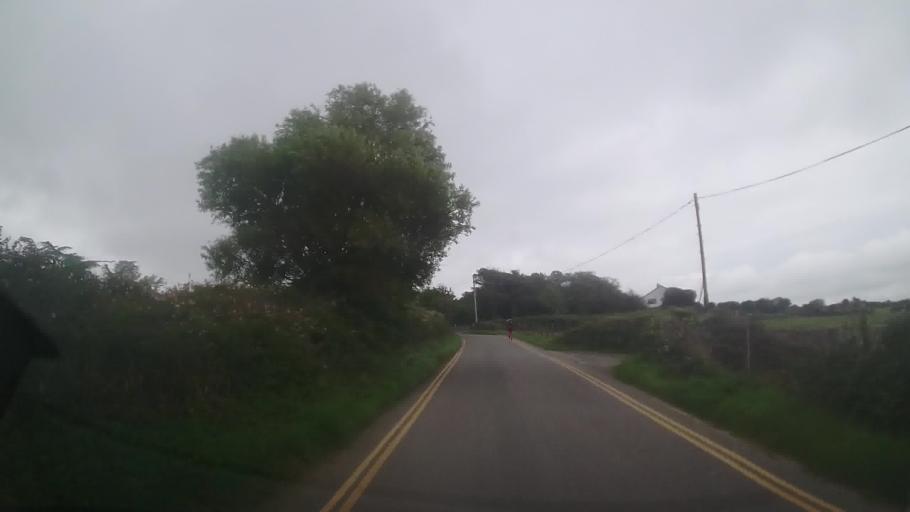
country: GB
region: Wales
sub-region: Gwynedd
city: Caernarfon
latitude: 53.1591
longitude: -4.3717
